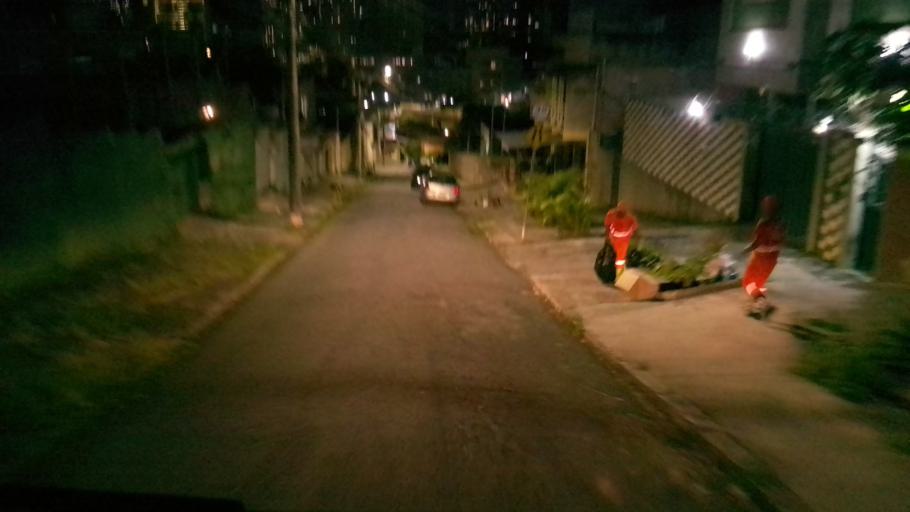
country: BR
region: Minas Gerais
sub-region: Belo Horizonte
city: Belo Horizonte
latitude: -19.9177
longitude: -43.9238
